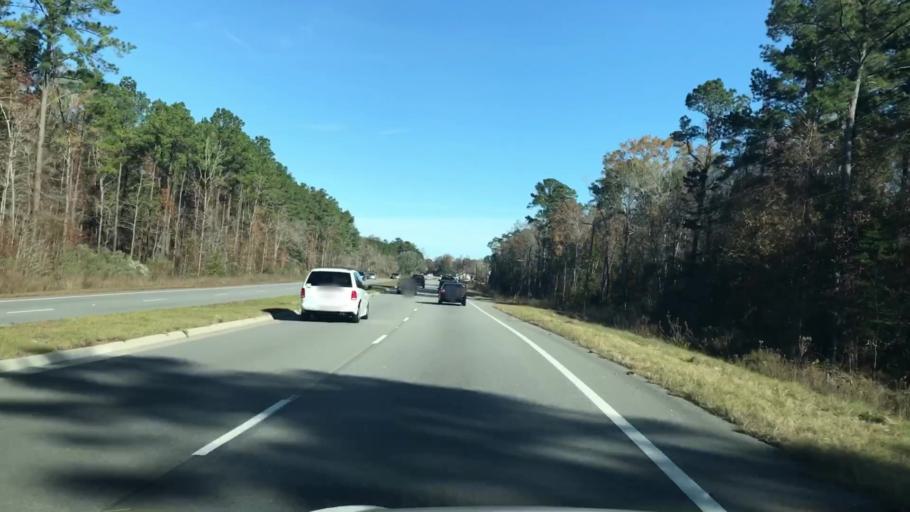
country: US
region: South Carolina
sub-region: Dorchester County
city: Centerville
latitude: 32.9530
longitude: -80.2018
